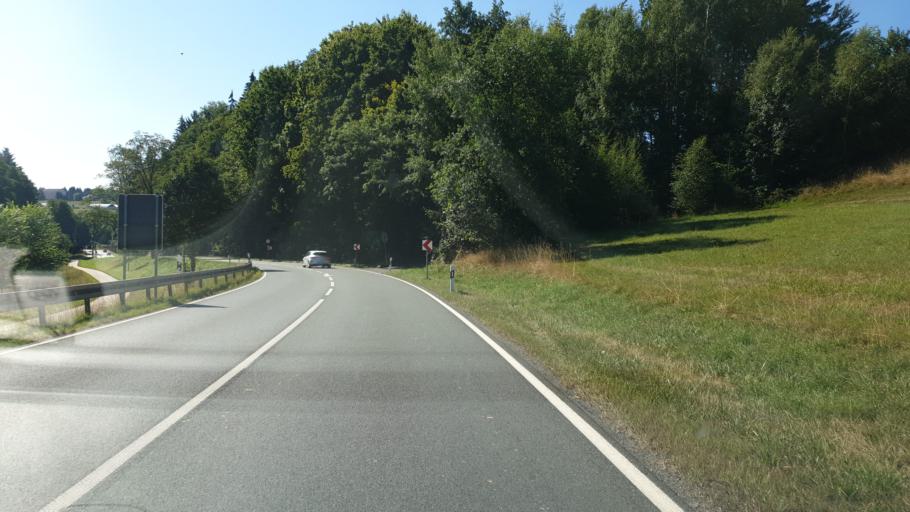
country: DE
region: Saxony
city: Lengenfeld
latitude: 50.5828
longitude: 12.3529
